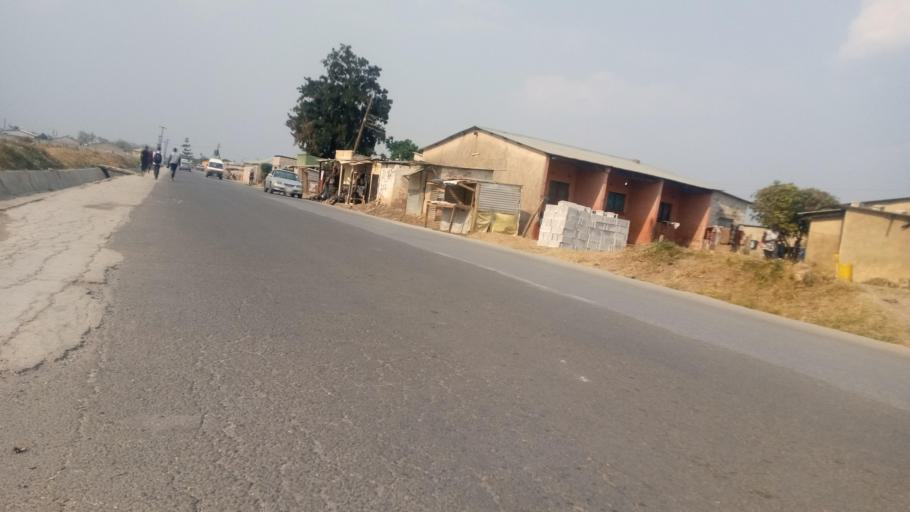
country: ZM
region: Lusaka
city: Lusaka
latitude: -15.4442
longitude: 28.3749
